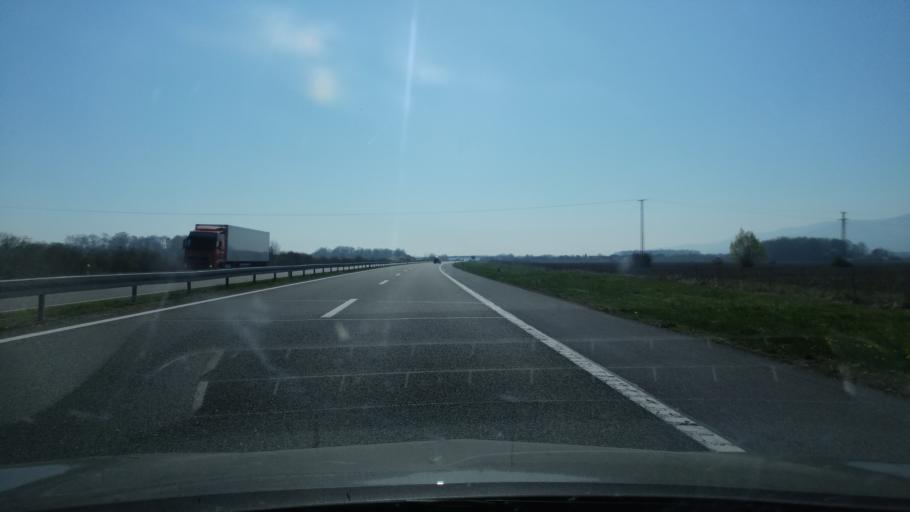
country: HR
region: Brodsko-Posavska
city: Batrina
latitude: 45.1857
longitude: 17.6382
